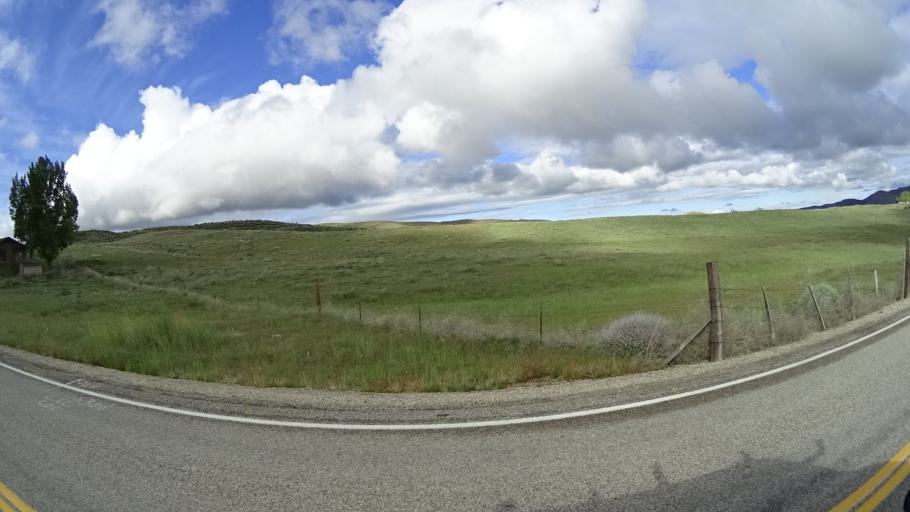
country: US
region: Idaho
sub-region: Ada County
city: Eagle
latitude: 43.7259
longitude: -116.2636
